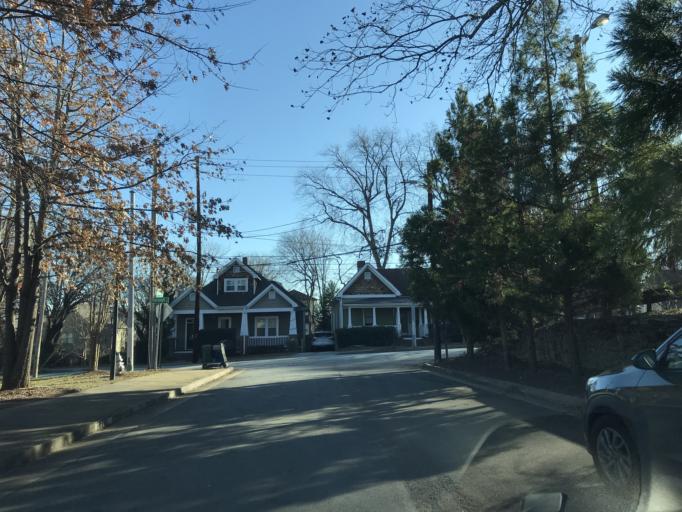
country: US
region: Georgia
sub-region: Fulton County
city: Atlanta
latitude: 33.7603
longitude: -84.3682
